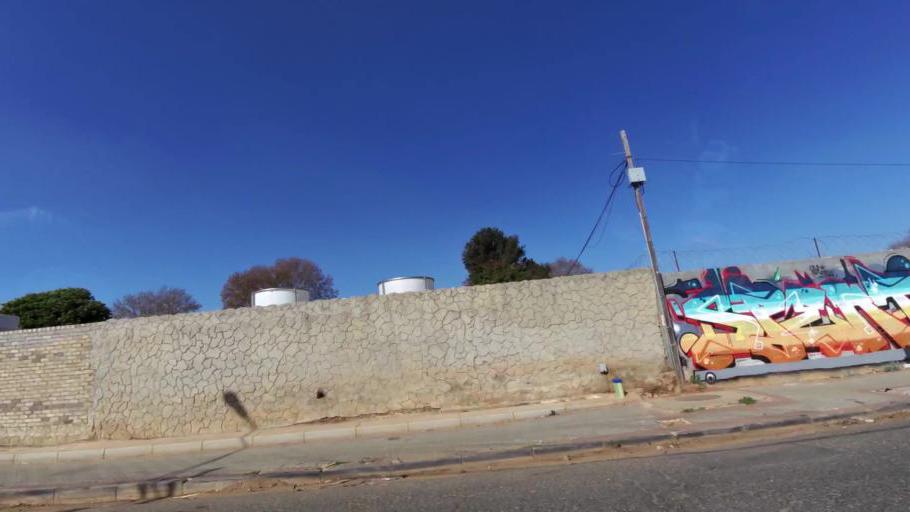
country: ZA
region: Gauteng
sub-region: City of Johannesburg Metropolitan Municipality
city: Johannesburg
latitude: -26.1809
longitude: 27.9804
